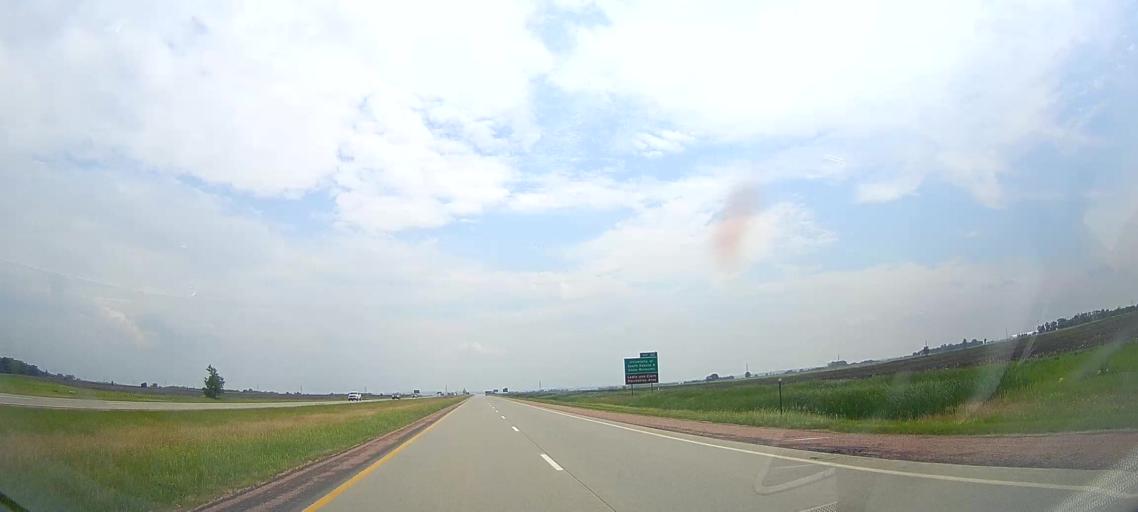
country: US
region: South Dakota
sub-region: Clay County
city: Vermillion
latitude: 42.8030
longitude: -96.7961
